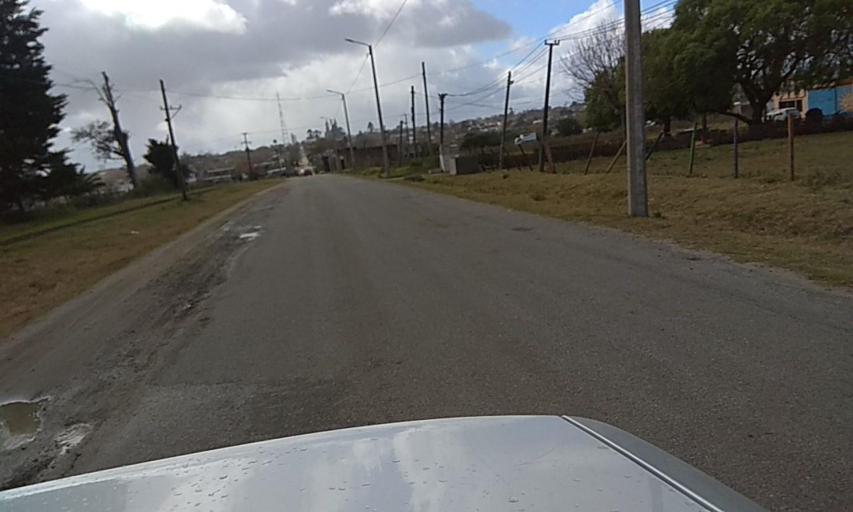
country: UY
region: Florida
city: Florida
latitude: -34.1089
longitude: -56.2245
